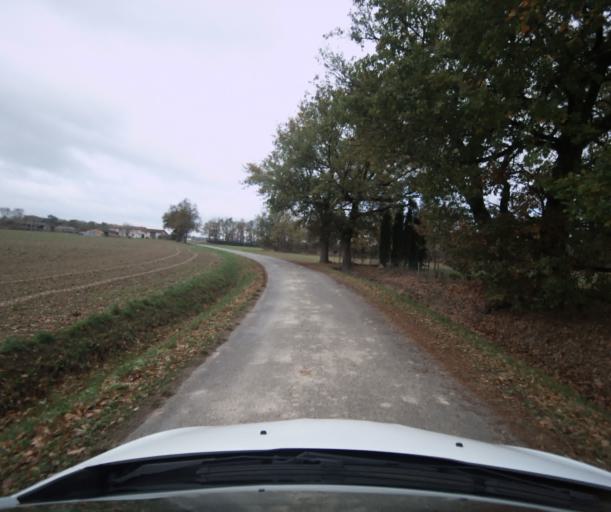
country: FR
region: Midi-Pyrenees
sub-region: Departement du Tarn-et-Garonne
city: Saint-Porquier
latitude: 44.0547
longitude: 1.1666
